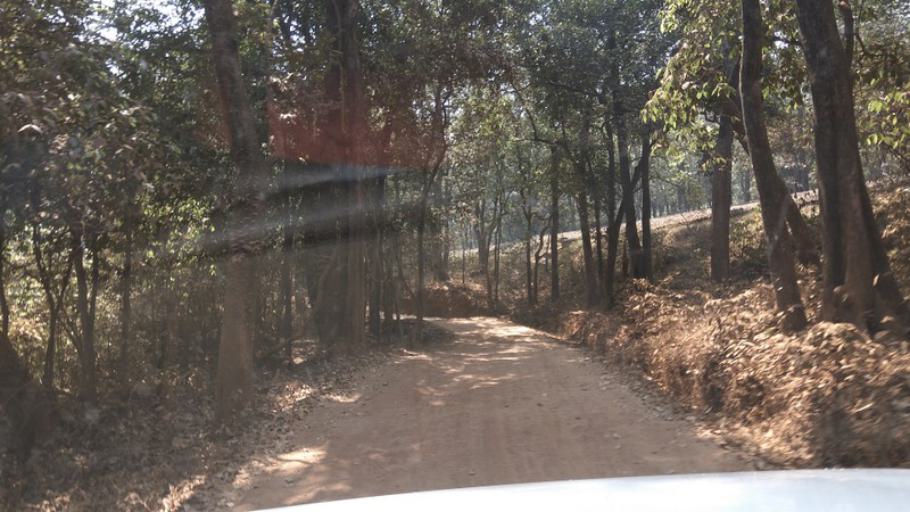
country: IN
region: Goa
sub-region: South Goa
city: Sanguem
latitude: 15.3275
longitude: 74.2820
